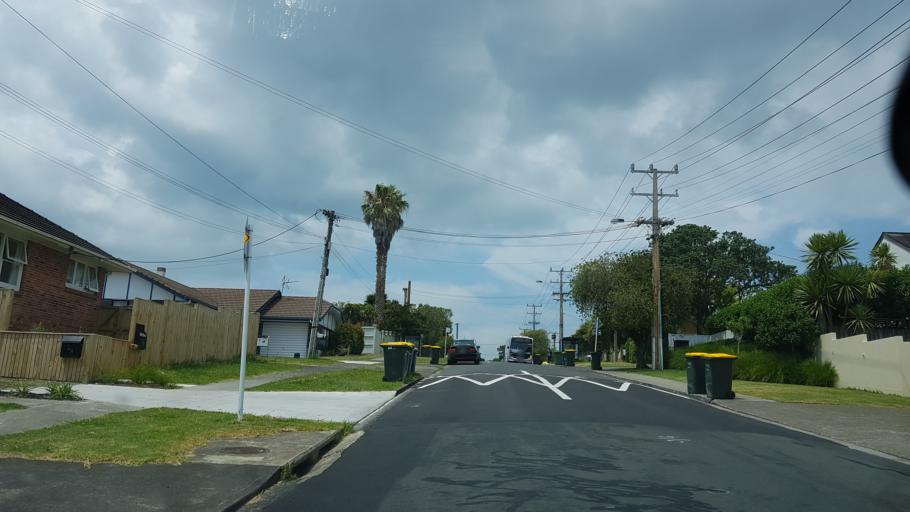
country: NZ
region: Auckland
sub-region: Auckland
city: North Shore
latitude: -36.8021
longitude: 174.7830
